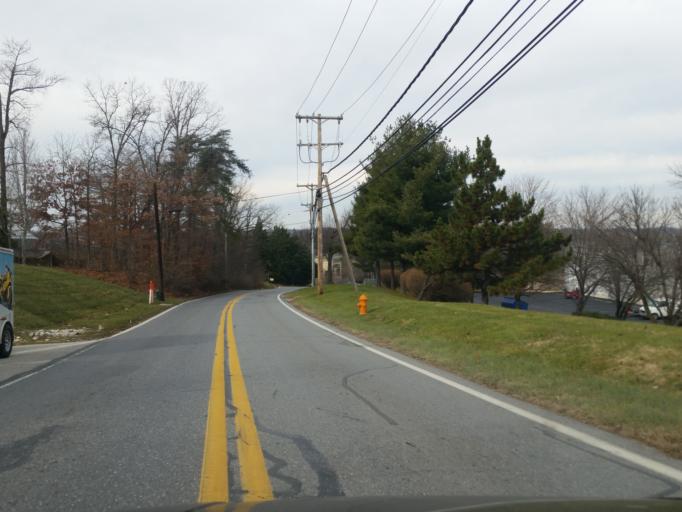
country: US
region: Maryland
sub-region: Howard County
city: Fort George G Mead Junction
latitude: 39.1336
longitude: -76.8006
